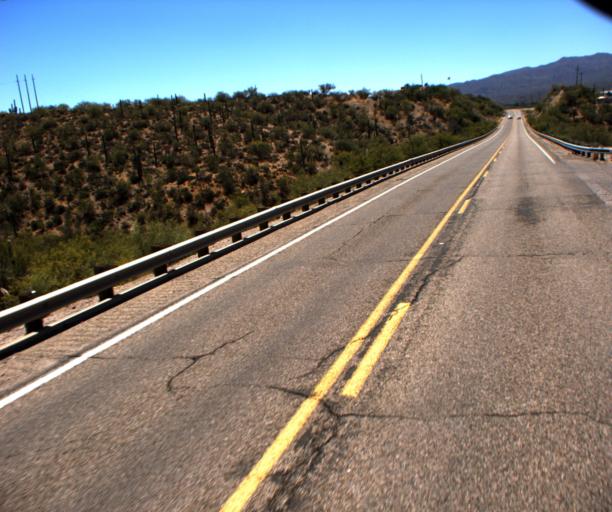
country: US
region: Arizona
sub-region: Pinal County
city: Kearny
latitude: 33.0828
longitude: -110.9260
